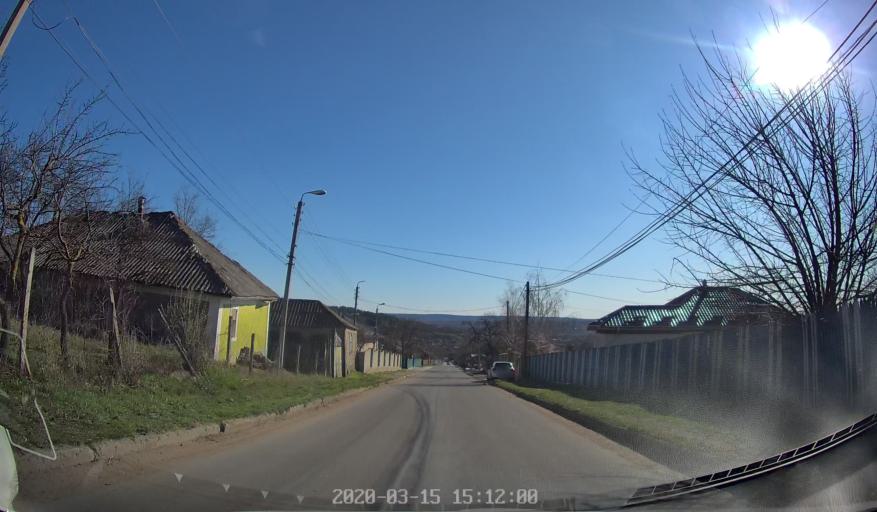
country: MD
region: Orhei
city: Orhei
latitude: 47.2590
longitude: 28.7745
